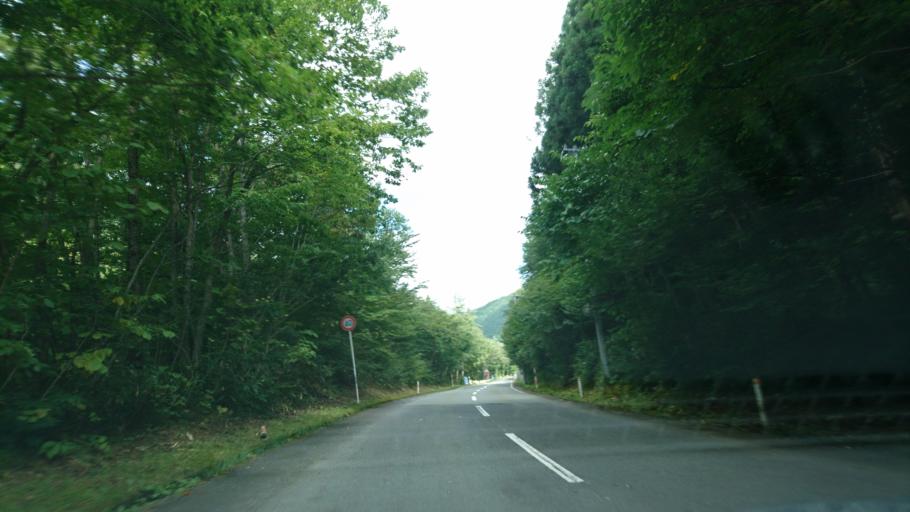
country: JP
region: Miyagi
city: Furukawa
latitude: 38.8578
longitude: 140.7784
